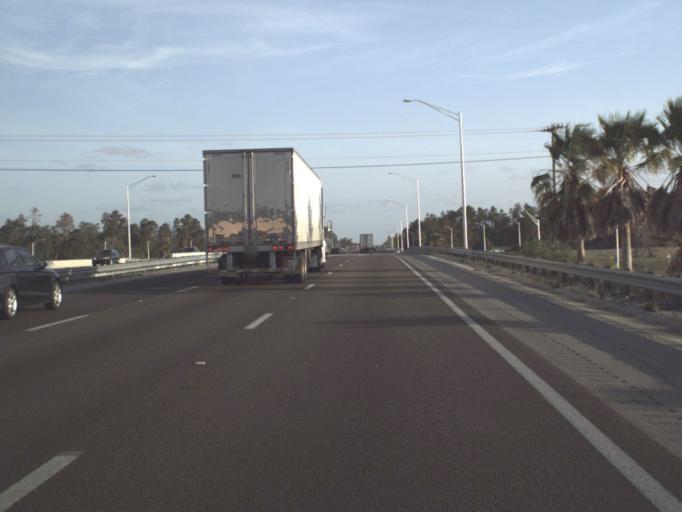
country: US
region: Florida
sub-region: Brevard County
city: Titusville
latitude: 28.6174
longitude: -80.8514
